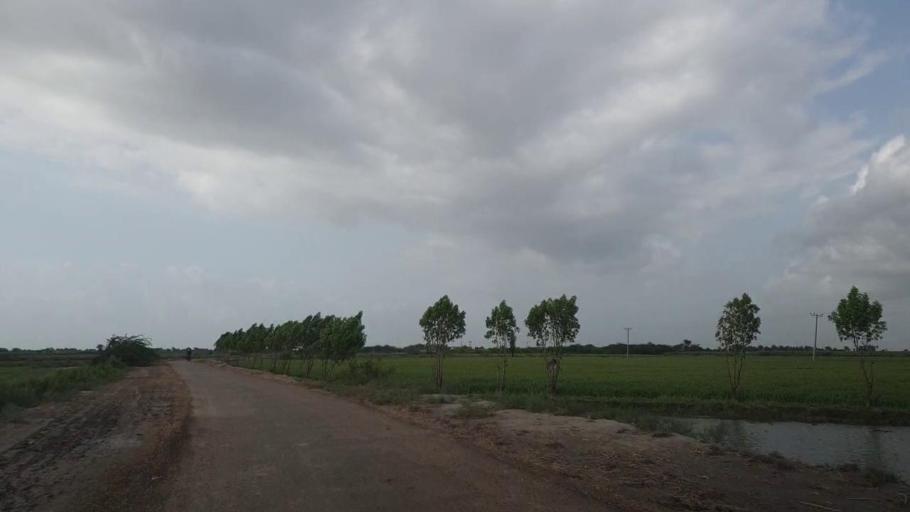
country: PK
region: Sindh
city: Kadhan
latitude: 24.5917
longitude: 69.0554
